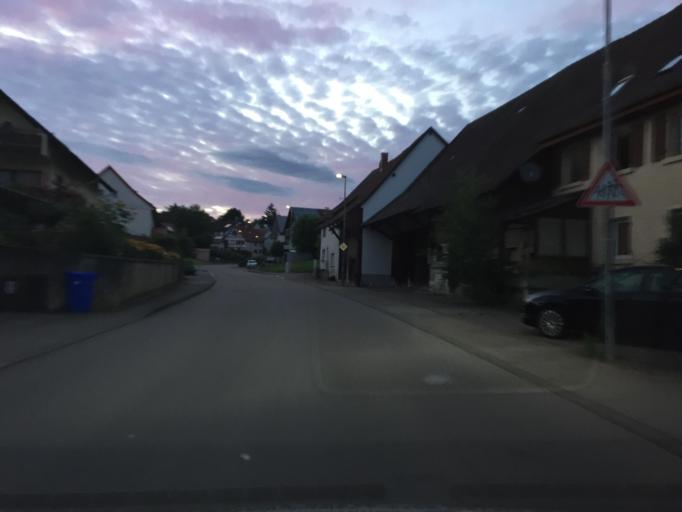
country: DE
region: Baden-Wuerttemberg
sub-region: Freiburg Region
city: Eggingen
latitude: 47.6584
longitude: 8.4212
